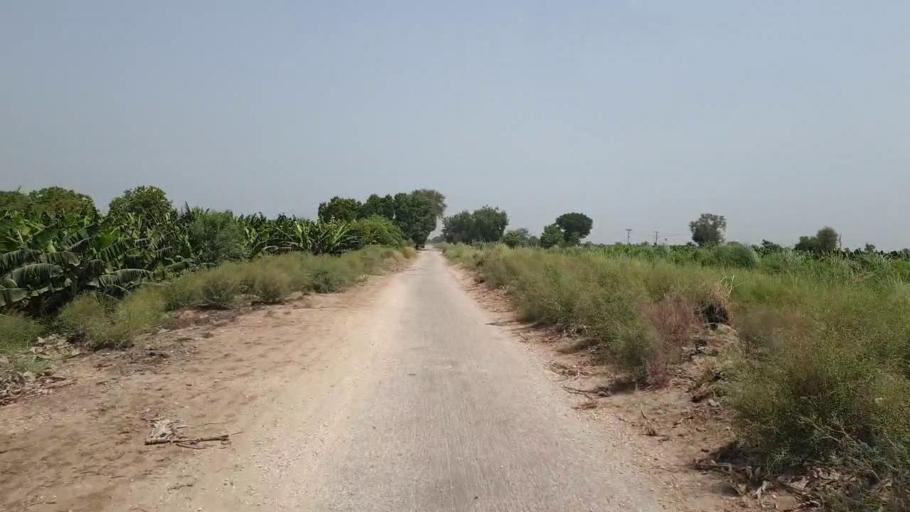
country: PK
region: Sindh
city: Nawabshah
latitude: 26.2809
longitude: 68.3119
